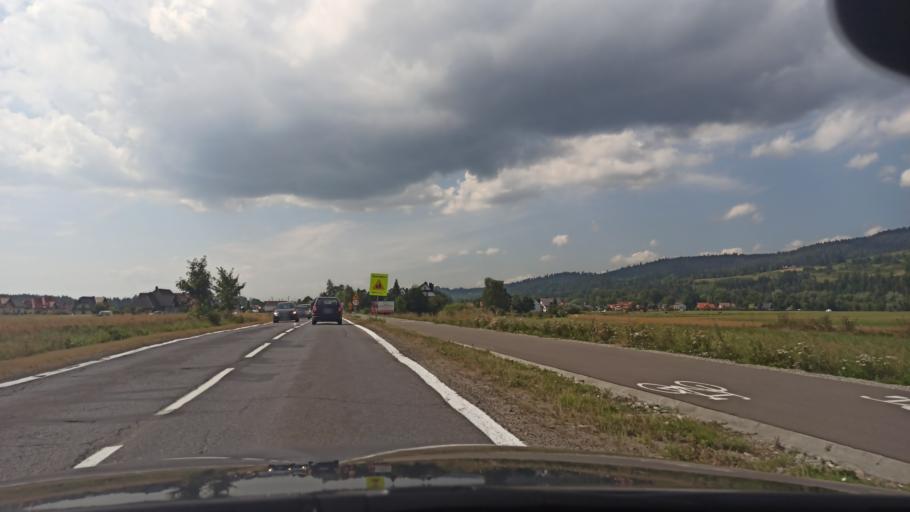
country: PL
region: Lesser Poland Voivodeship
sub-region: Powiat nowotarski
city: Lopuszna
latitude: 49.4729
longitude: 20.1810
